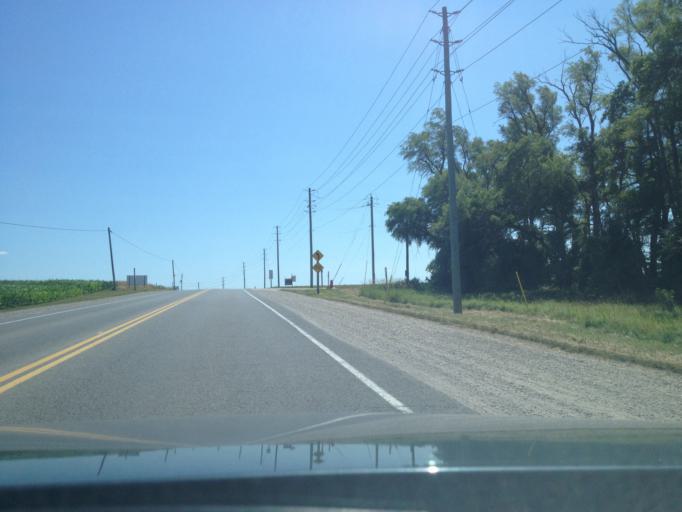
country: CA
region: Ontario
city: Waterloo
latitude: 43.5351
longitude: -80.5121
